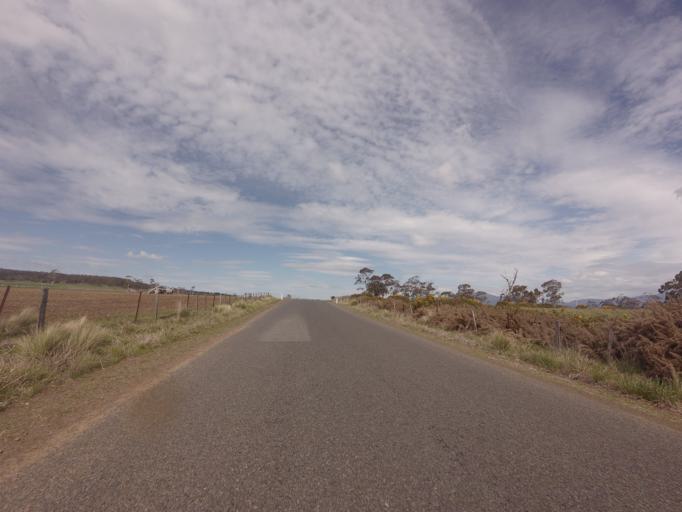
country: AU
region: Tasmania
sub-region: Northern Midlands
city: Longford
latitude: -41.7398
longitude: 147.2022
